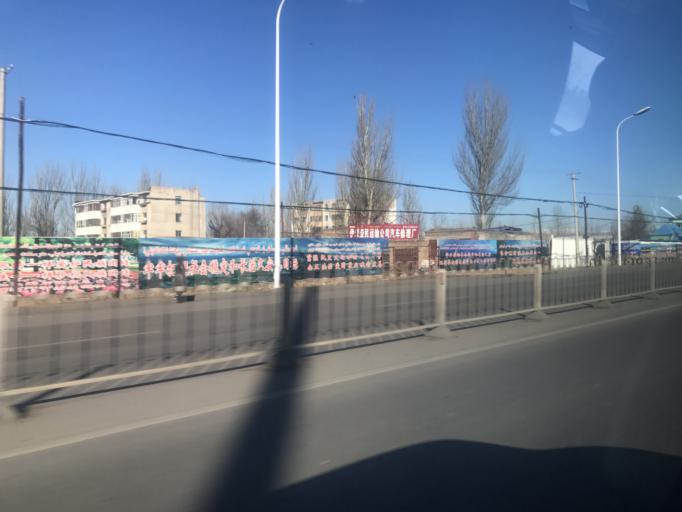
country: CN
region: Xinjiang Uygur Zizhiqu
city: Dadamtu
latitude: 43.9545
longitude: 81.3570
